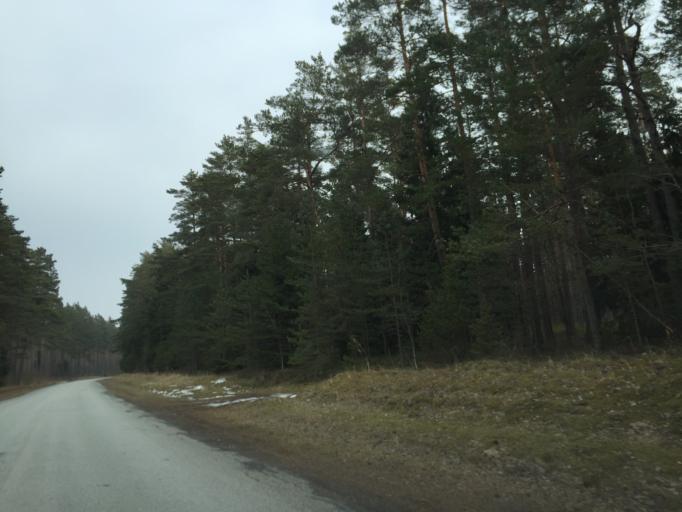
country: LV
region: Salacgrivas
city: Ainazi
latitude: 57.9837
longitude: 24.4181
